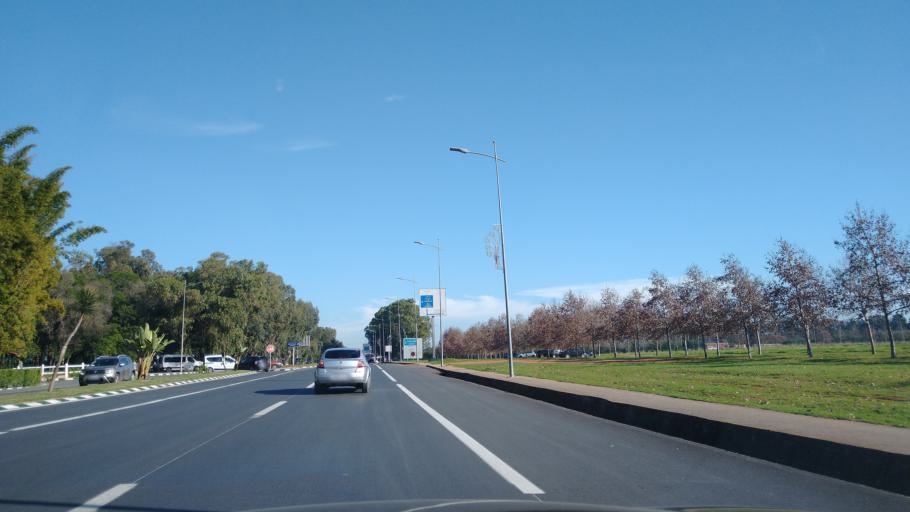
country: MA
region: Rabat-Sale-Zemmour-Zaer
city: Sale
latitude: 34.0292
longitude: -6.7378
